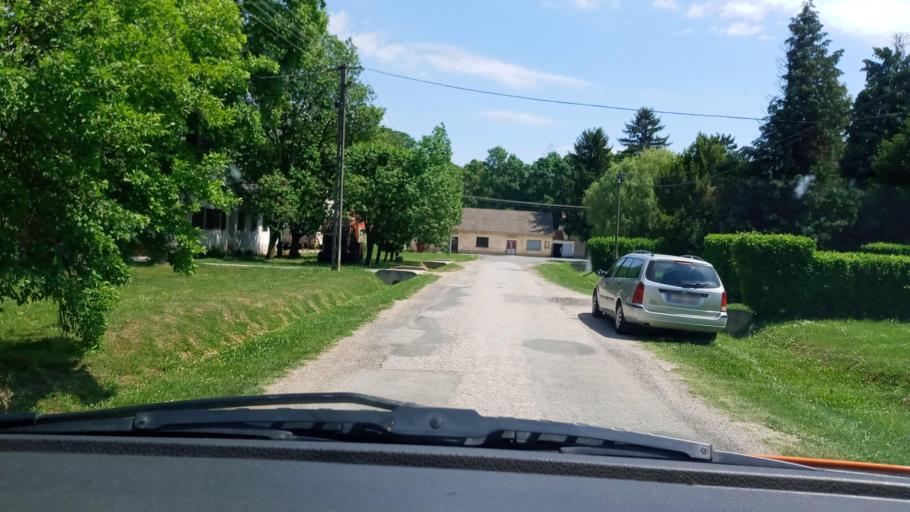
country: HU
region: Baranya
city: Harkany
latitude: 45.8353
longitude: 18.2054
